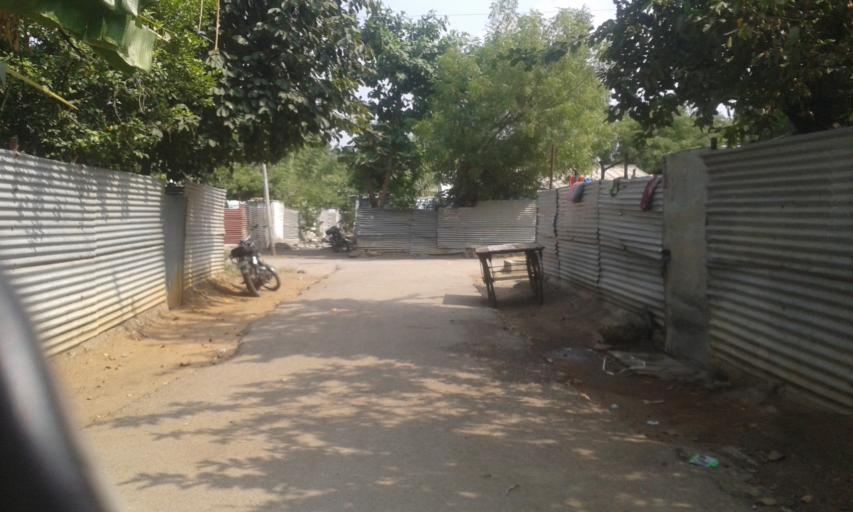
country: IN
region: Karnataka
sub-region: Raichur
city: Lingsugur
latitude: 16.1935
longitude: 76.6614
